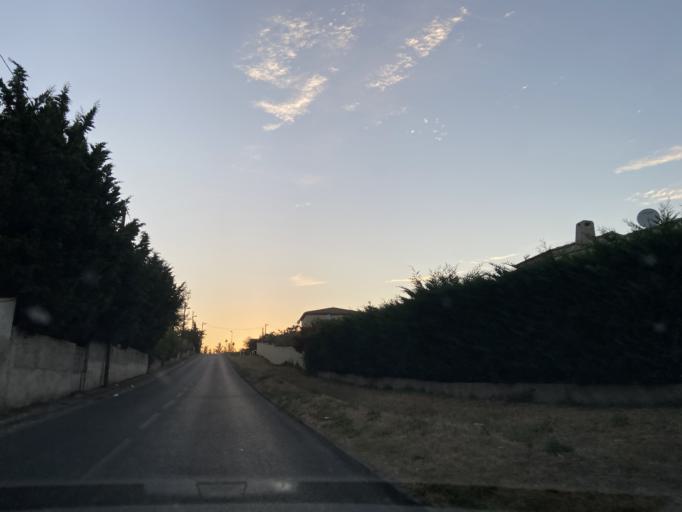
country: FR
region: Provence-Alpes-Cote d'Azur
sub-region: Departement des Bouches-du-Rhone
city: Plan-de-Cuques
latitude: 43.3256
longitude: 5.4505
